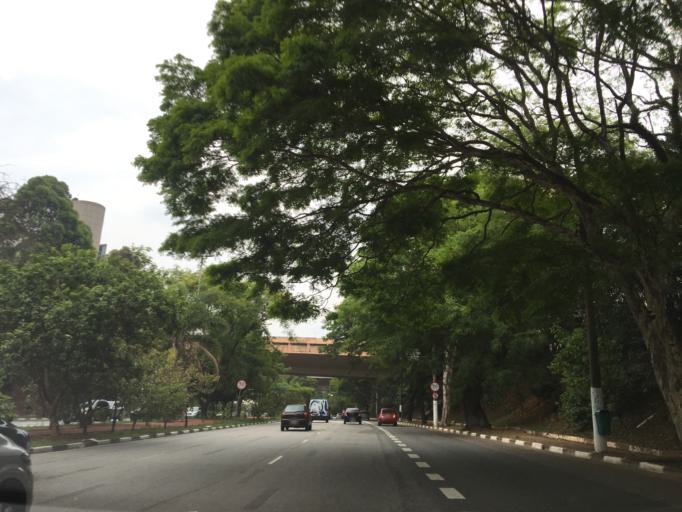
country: BR
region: Sao Paulo
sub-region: Sao Paulo
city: Sao Paulo
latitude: -23.5527
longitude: -46.6785
